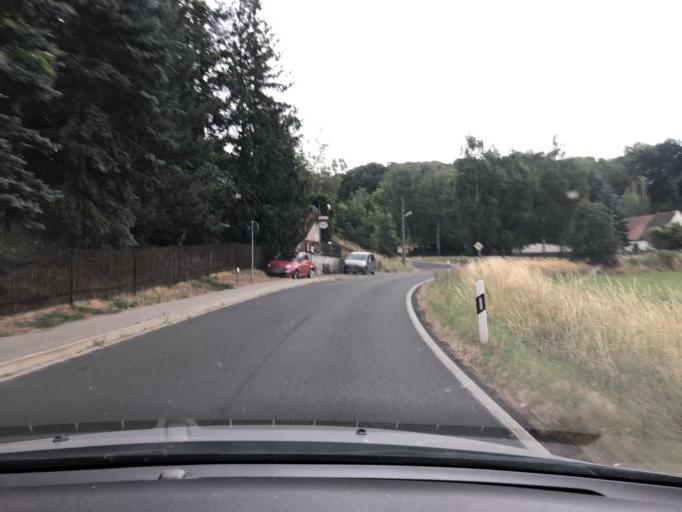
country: DE
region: Saxony
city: Frohburg
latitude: 51.0176
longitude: 12.5799
